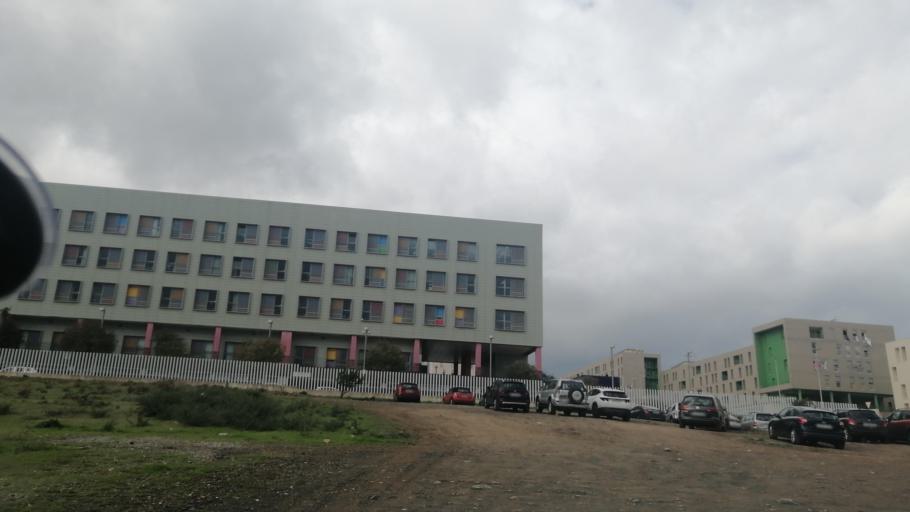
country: ES
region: Ceuta
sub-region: Ceuta
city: Ceuta
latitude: 35.8802
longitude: -5.3401
